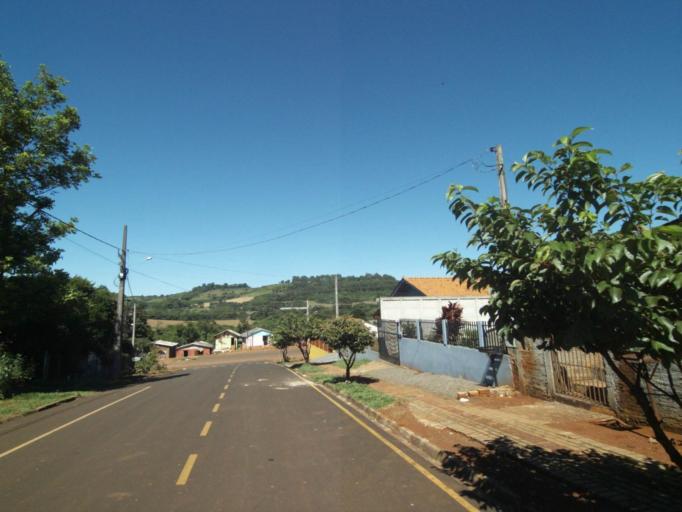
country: BR
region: Santa Catarina
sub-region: Sao Lourenco Do Oeste
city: Sao Lourenco dOeste
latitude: -26.2729
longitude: -52.7798
